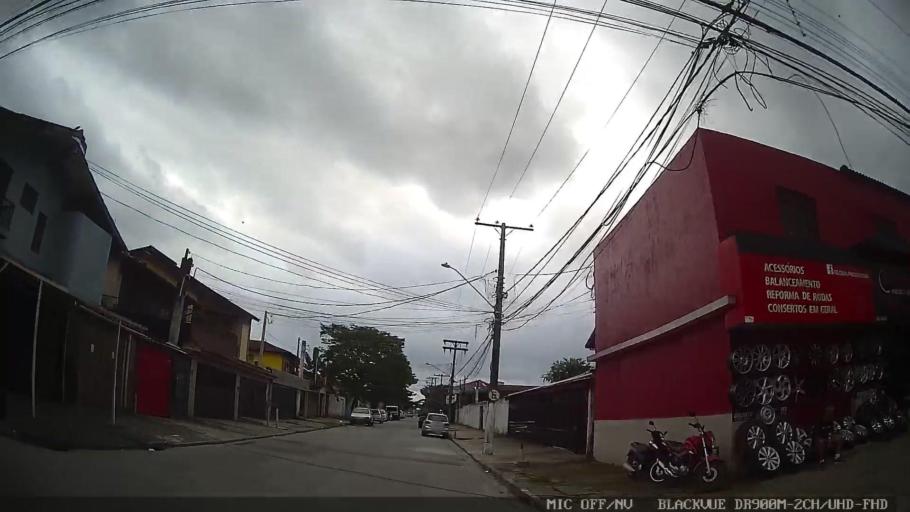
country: BR
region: Sao Paulo
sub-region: Guaruja
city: Guaruja
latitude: -23.9962
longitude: -46.2734
